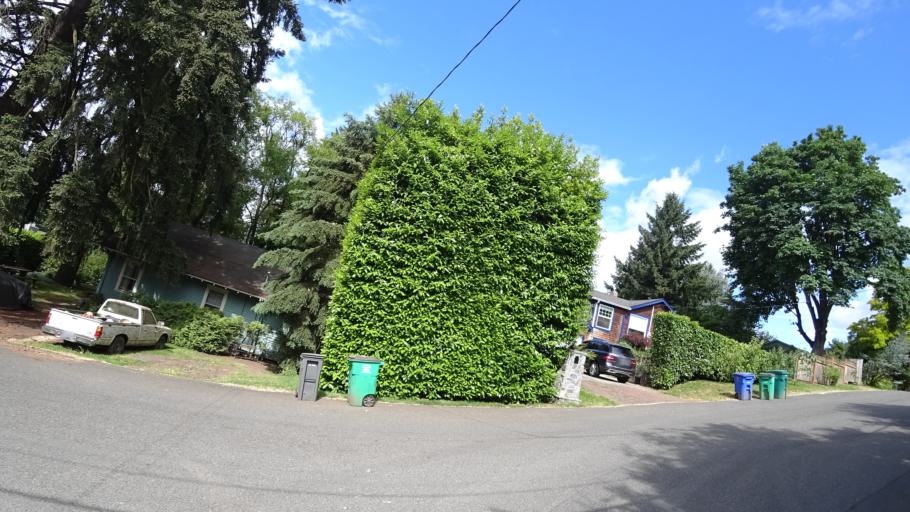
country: US
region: Oregon
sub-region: Clackamas County
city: Lake Oswego
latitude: 45.4603
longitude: -122.6869
